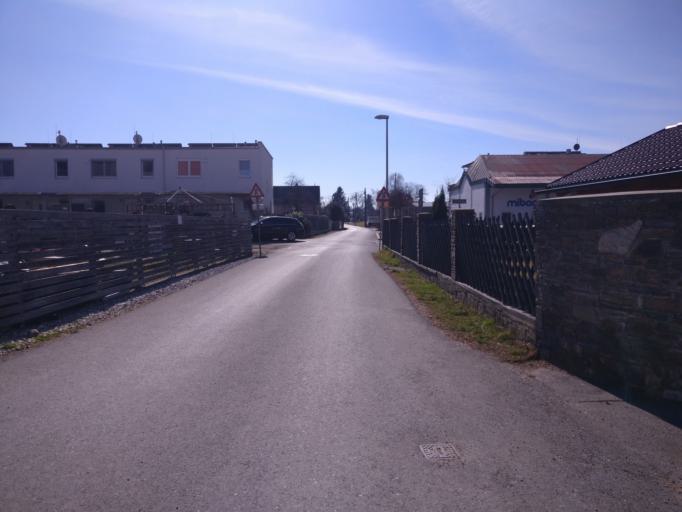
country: AT
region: Styria
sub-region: Politischer Bezirk Graz-Umgebung
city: Feldkirchen bei Graz
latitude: 47.0224
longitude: 15.4447
